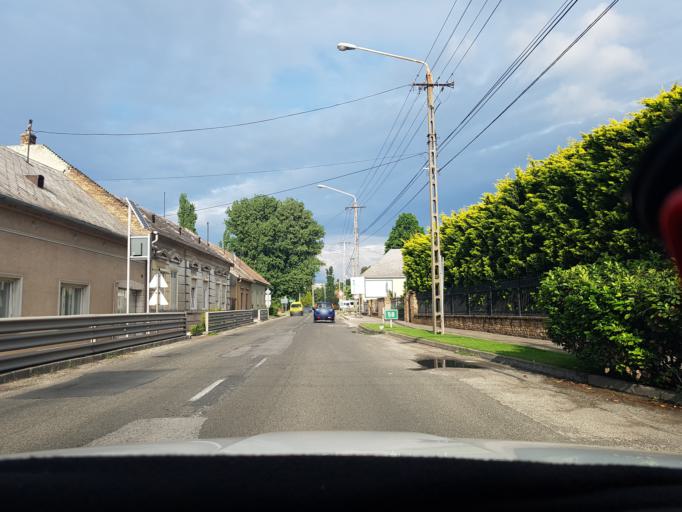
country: HU
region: Komarom-Esztergom
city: Labatlan
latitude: 47.7496
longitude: 18.4901
